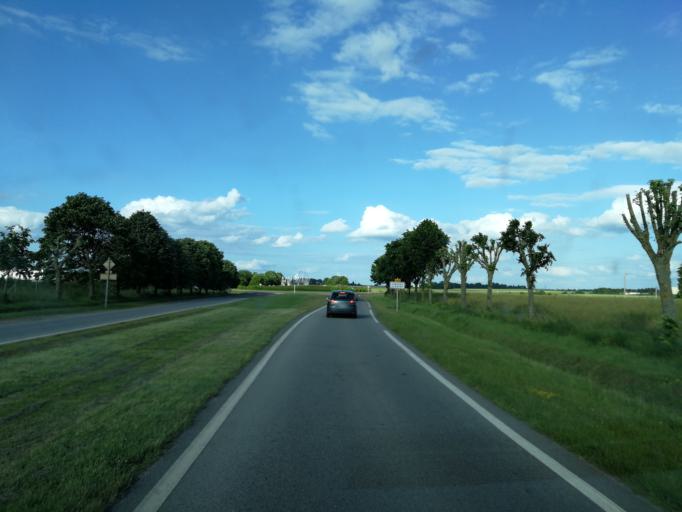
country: FR
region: Haute-Normandie
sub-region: Departement de l'Eure
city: Conches-en-Ouche
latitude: 48.9515
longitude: 0.9439
